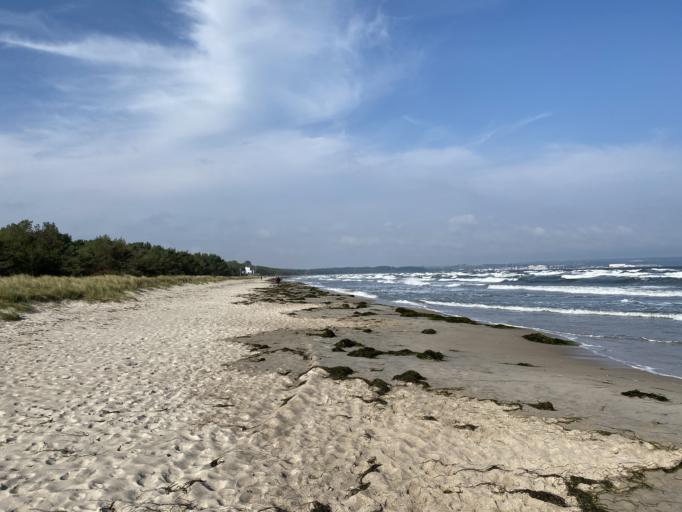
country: DE
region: Mecklenburg-Vorpommern
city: Ostseebad Binz
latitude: 54.4442
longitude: 13.5756
